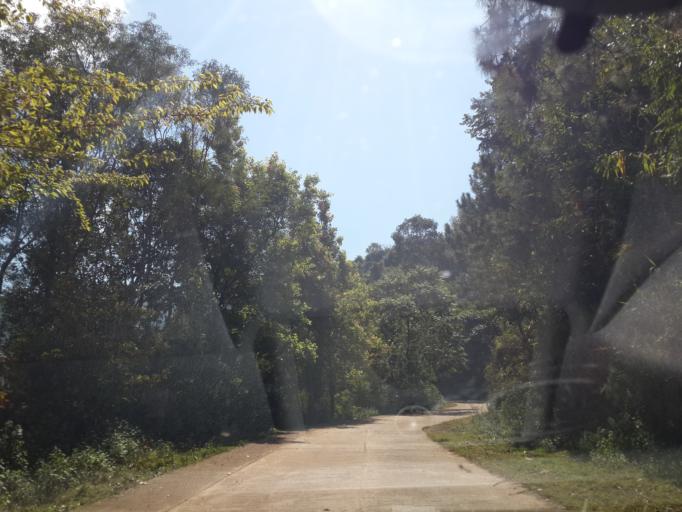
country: TH
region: Chiang Mai
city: Fang
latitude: 19.9245
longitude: 99.0511
